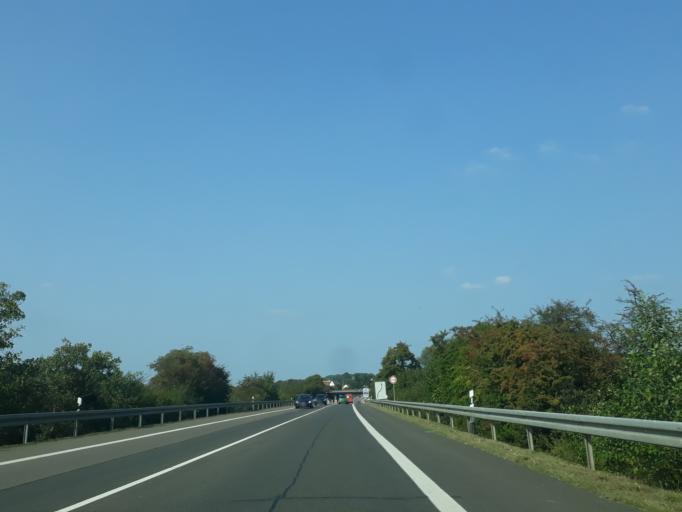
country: DE
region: Saarland
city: Blieskastel
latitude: 49.2633
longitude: 7.3086
